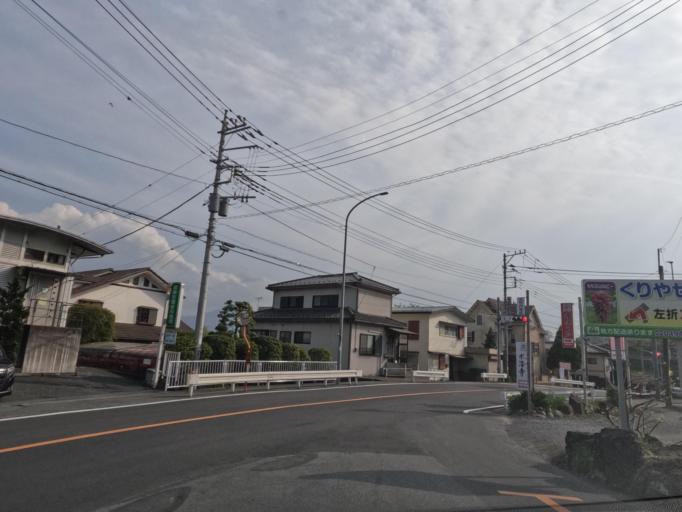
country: JP
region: Saitama
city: Chichibu
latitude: 36.0793
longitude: 139.0927
